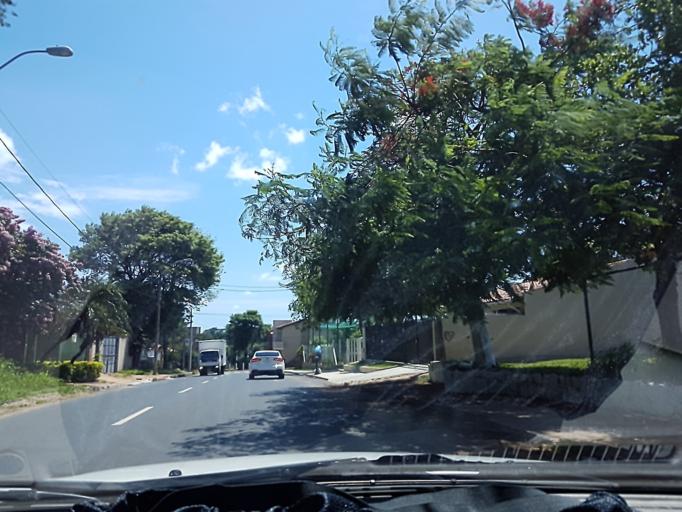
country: PY
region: Asuncion
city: Asuncion
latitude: -25.2711
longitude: -57.5753
